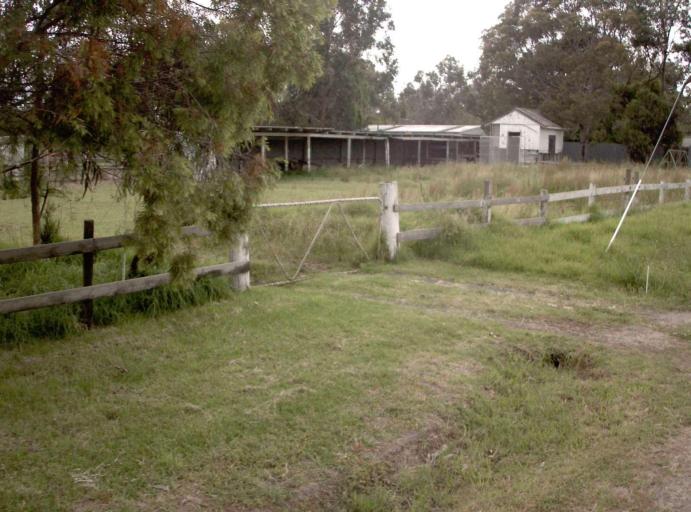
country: AU
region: Victoria
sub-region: Bass Coast
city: Cowes
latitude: -38.4206
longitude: 145.4377
